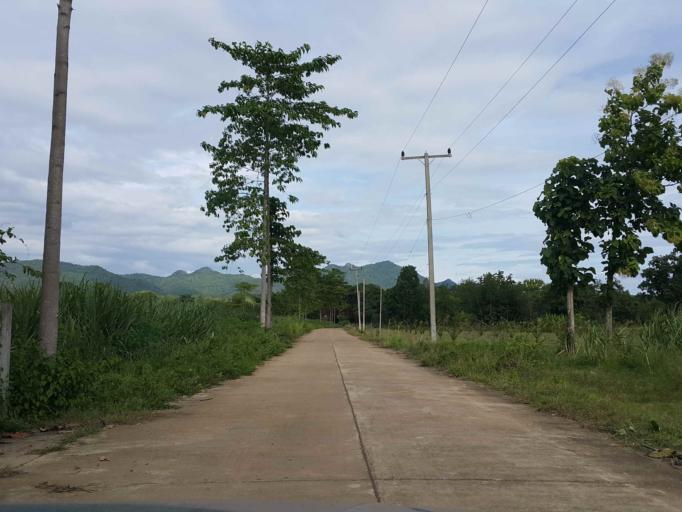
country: TH
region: Sukhothai
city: Thung Saliam
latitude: 17.2301
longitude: 99.5186
